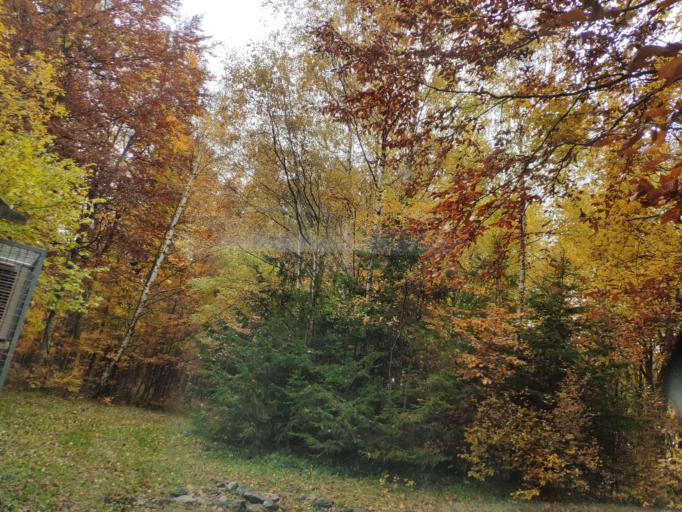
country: SK
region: Kosicky
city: Medzev
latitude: 48.7348
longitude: 21.0053
